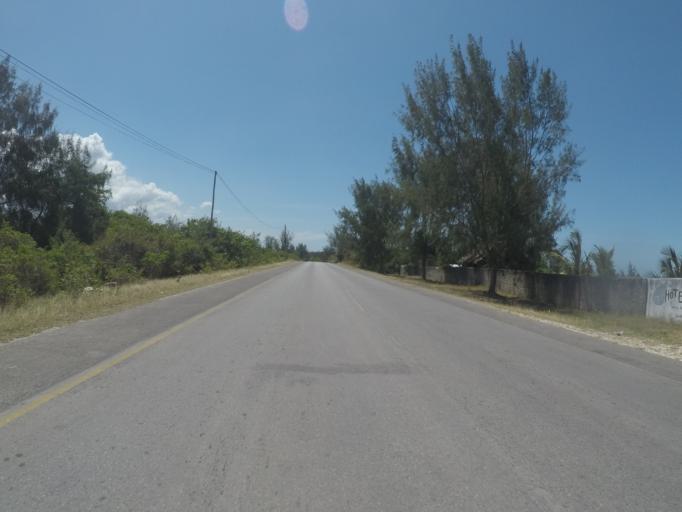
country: TZ
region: Zanzibar Central/South
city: Nganane
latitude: -6.2862
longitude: 39.5363
